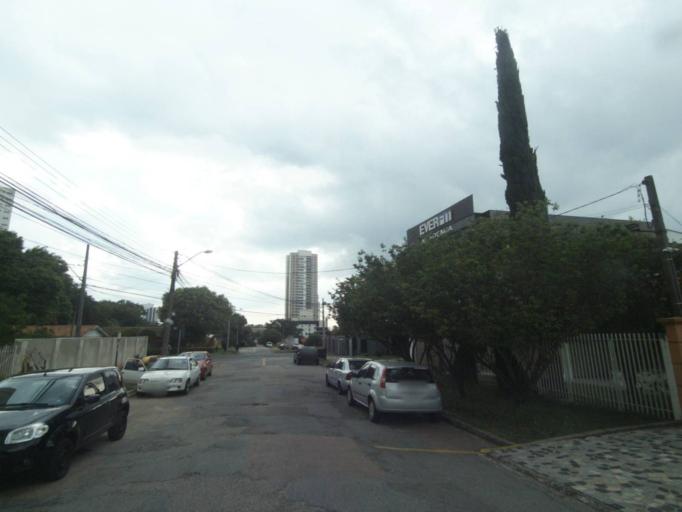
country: BR
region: Parana
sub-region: Curitiba
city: Curitiba
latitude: -25.4402
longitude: -49.3483
